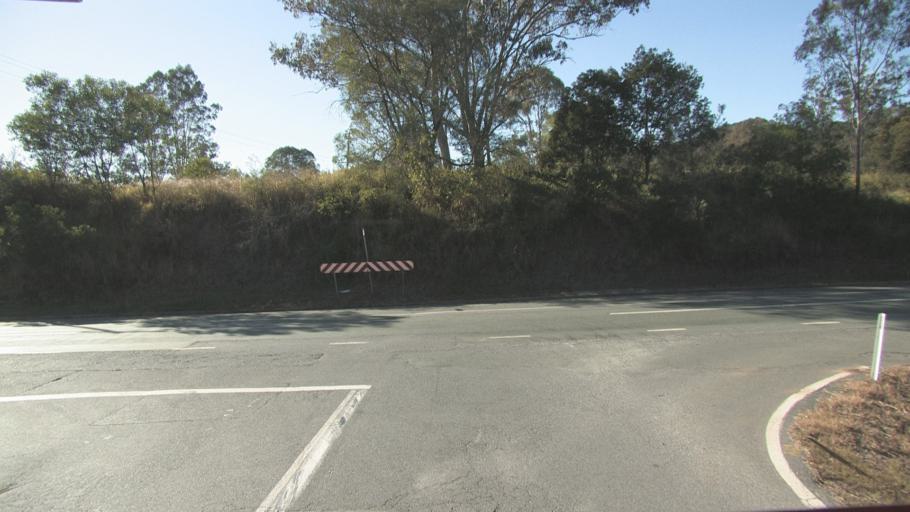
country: AU
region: Queensland
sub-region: Logan
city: Windaroo
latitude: -27.7959
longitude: 153.1769
